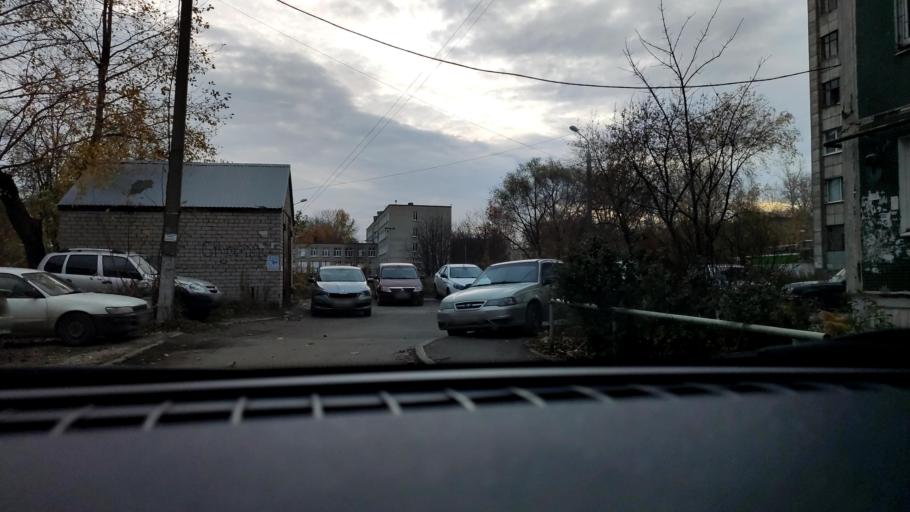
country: RU
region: Perm
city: Perm
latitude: 57.9806
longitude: 56.2900
